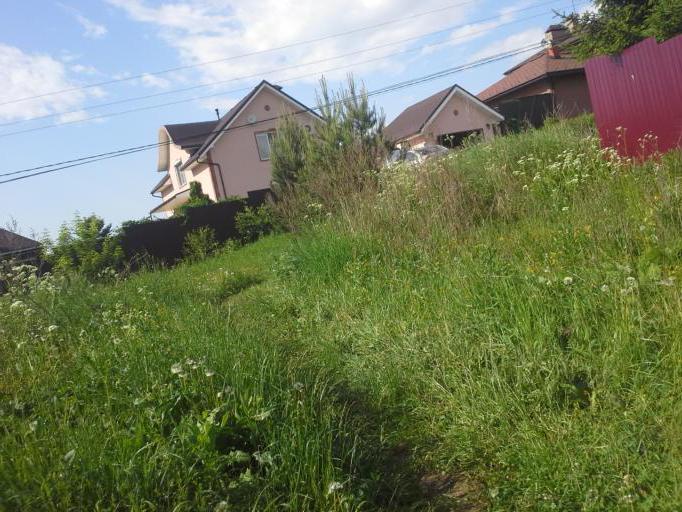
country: RU
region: Moskovskaya
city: Filimonki
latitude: 55.5762
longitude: 37.3462
